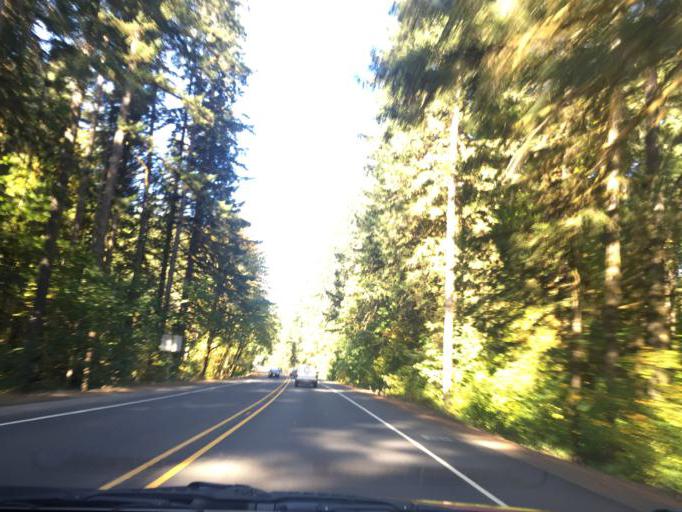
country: US
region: Oregon
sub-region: Columbia County
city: Vernonia
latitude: 45.7736
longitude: -123.3248
